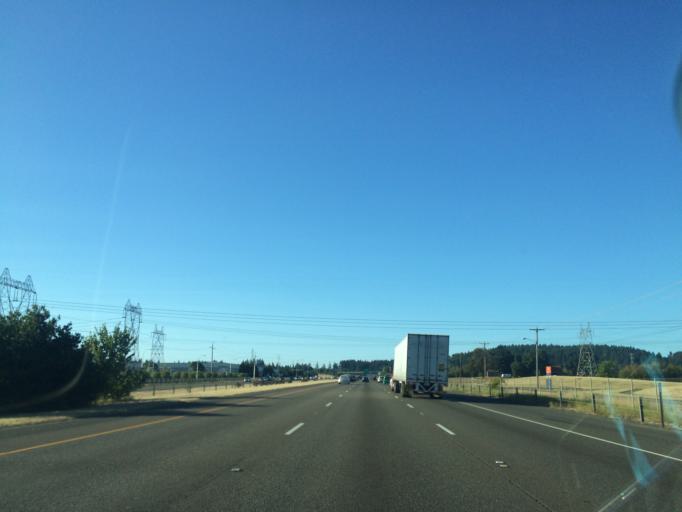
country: US
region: Oregon
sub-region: Clackamas County
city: Wilsonville
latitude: 45.3259
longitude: -122.7691
